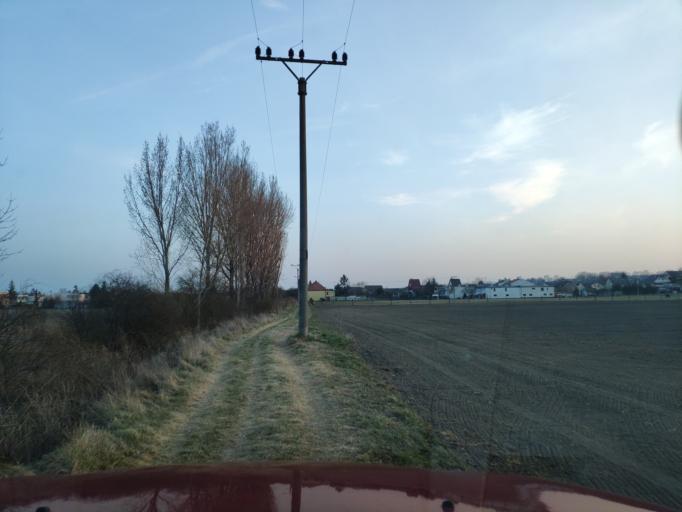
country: SK
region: Trnavsky
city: Leopoldov
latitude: 48.4426
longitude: 17.7127
